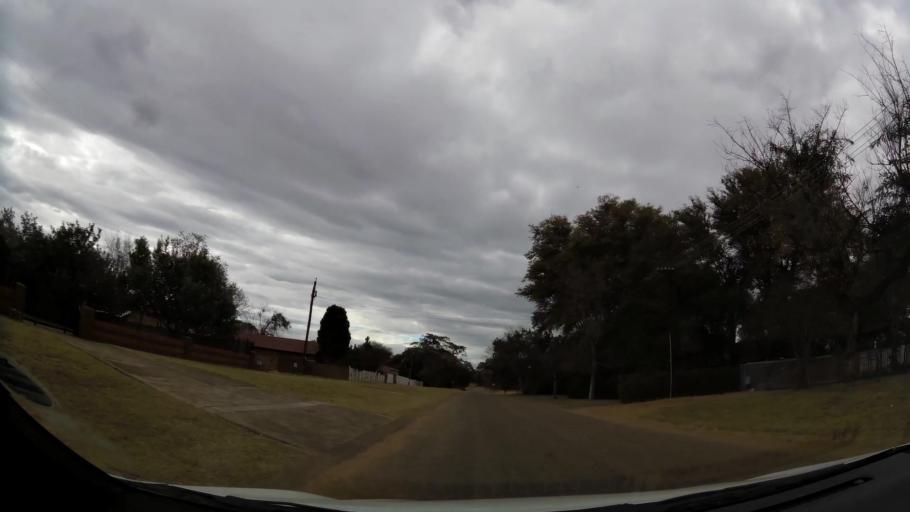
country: ZA
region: Limpopo
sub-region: Waterberg District Municipality
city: Modimolle
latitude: -24.7061
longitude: 28.4153
